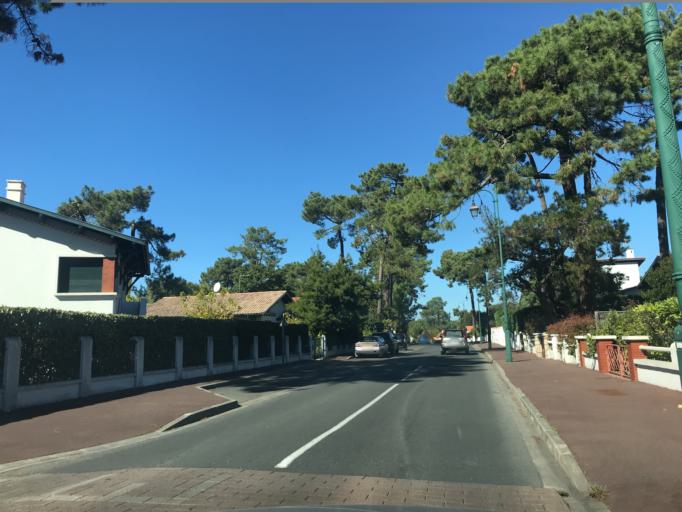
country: FR
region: Aquitaine
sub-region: Departement de la Gironde
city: Arcachon
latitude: 44.6499
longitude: -1.1795
